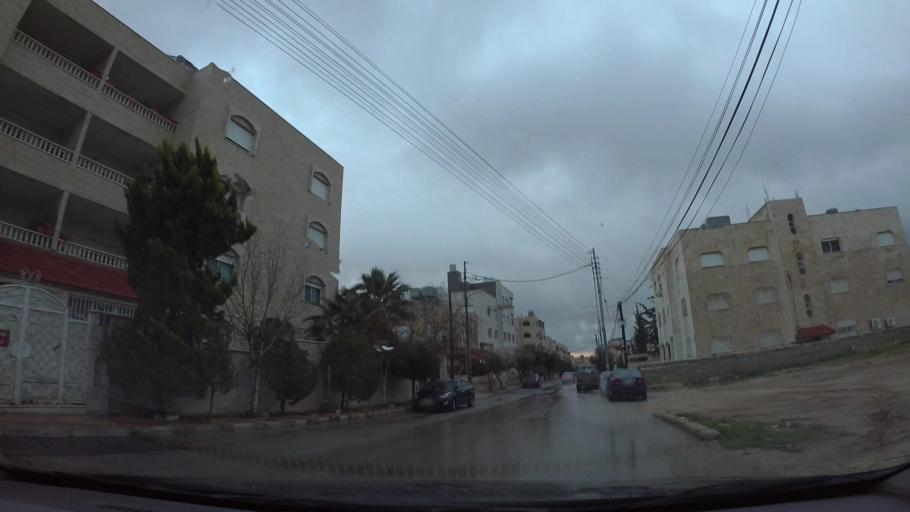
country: JO
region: Amman
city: Amman
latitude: 31.9993
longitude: 35.9271
